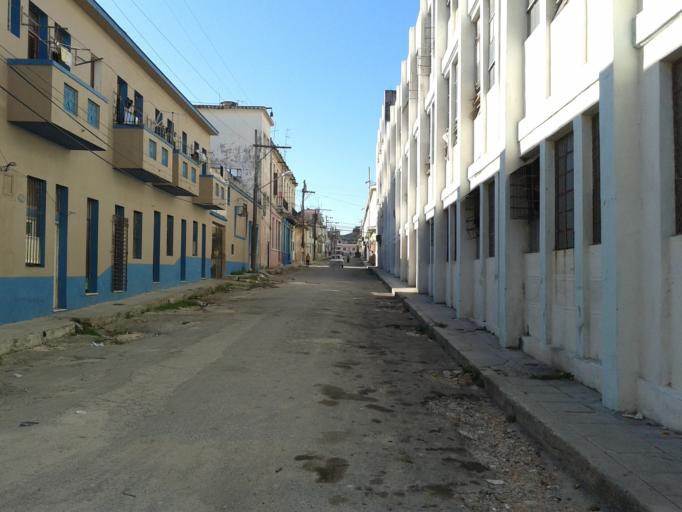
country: CU
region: La Habana
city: Cerro
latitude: 23.1207
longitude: -82.3754
